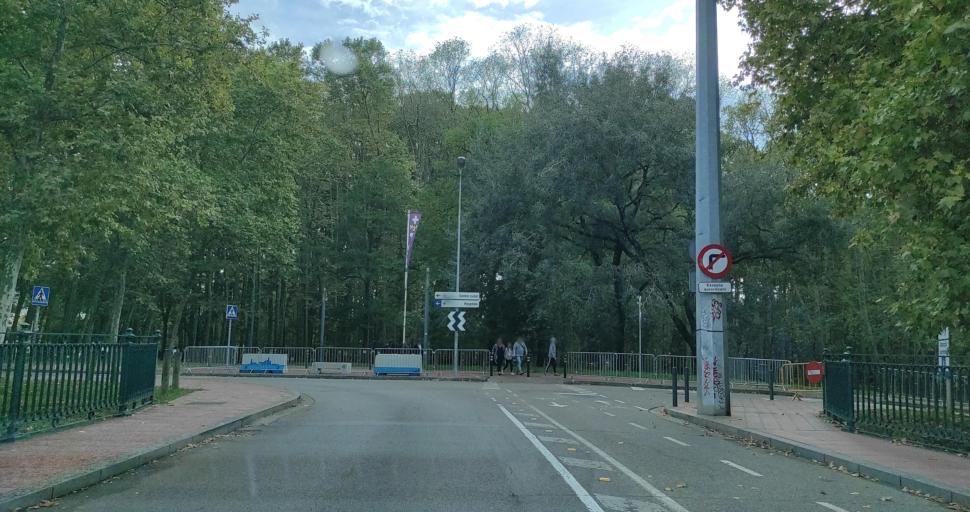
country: ES
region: Catalonia
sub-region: Provincia de Girona
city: Girona
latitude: 41.9900
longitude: 2.8192
